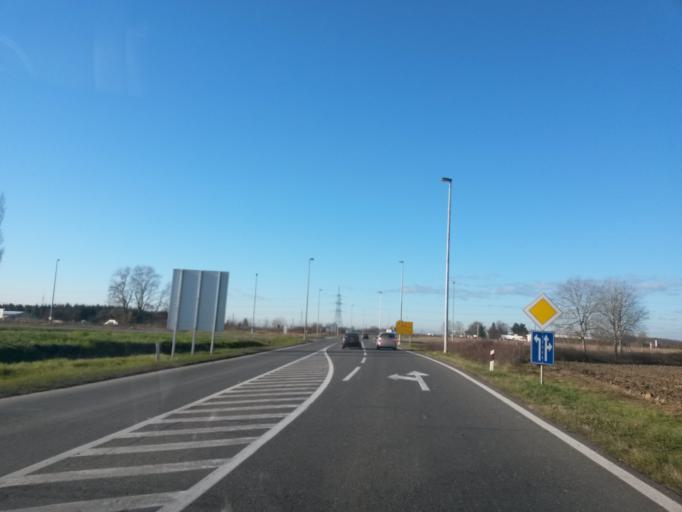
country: HR
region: Osjecko-Baranjska
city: Josipovac
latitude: 45.5855
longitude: 18.5621
